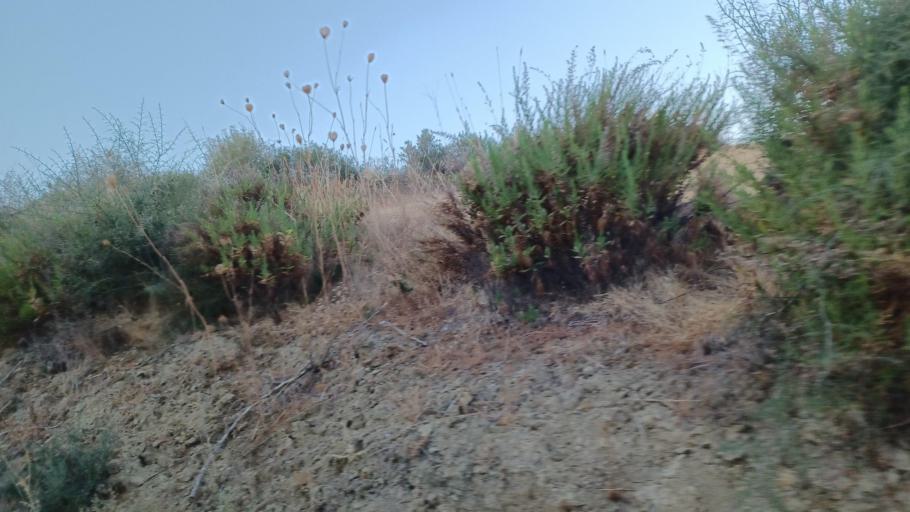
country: CY
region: Pafos
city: Polis
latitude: 34.9944
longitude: 32.4714
